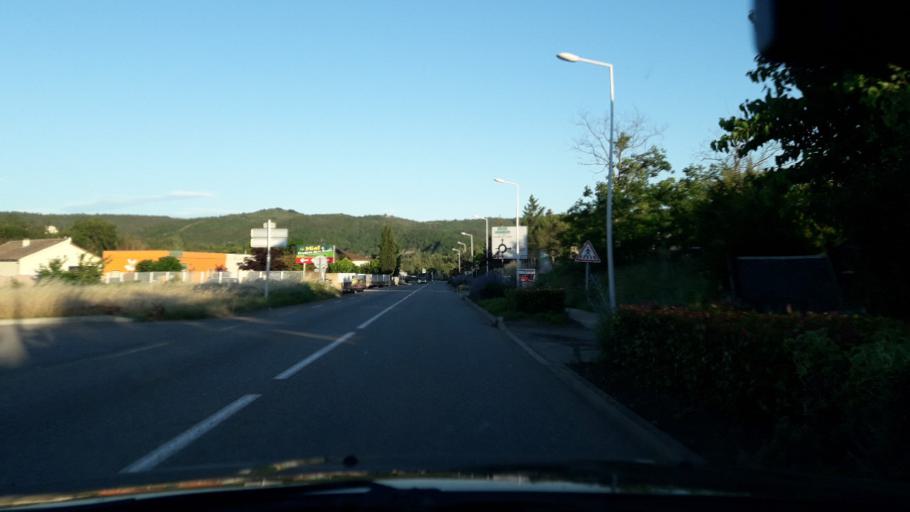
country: FR
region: Rhone-Alpes
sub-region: Departement de l'Ardeche
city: Lavilledieu
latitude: 44.5694
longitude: 4.4602
